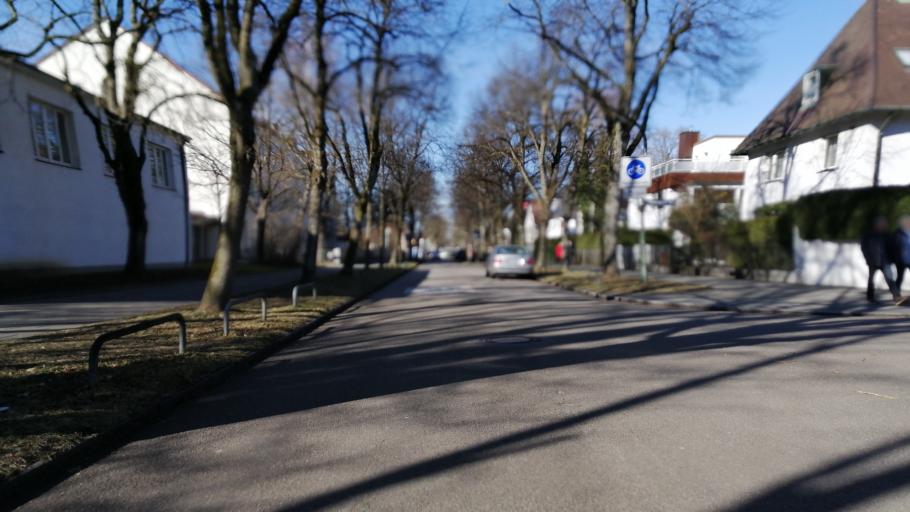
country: DE
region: Bavaria
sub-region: Upper Bavaria
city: Neuried
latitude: 48.1093
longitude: 11.5080
